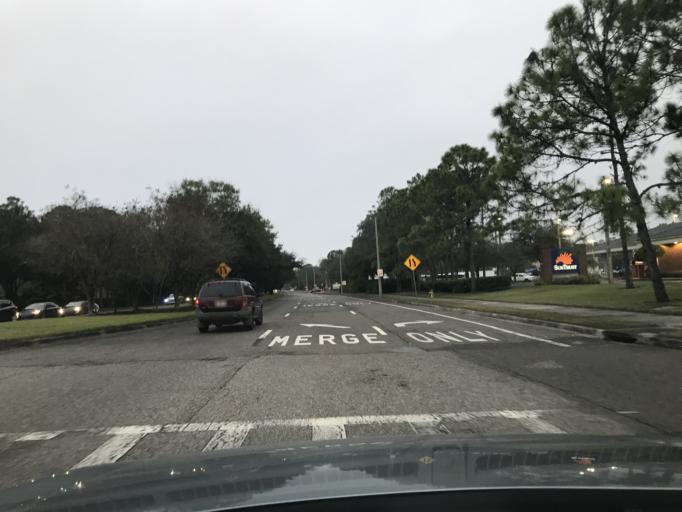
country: US
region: Florida
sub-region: Hillsborough County
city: Westchase
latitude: 28.0556
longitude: -82.6237
